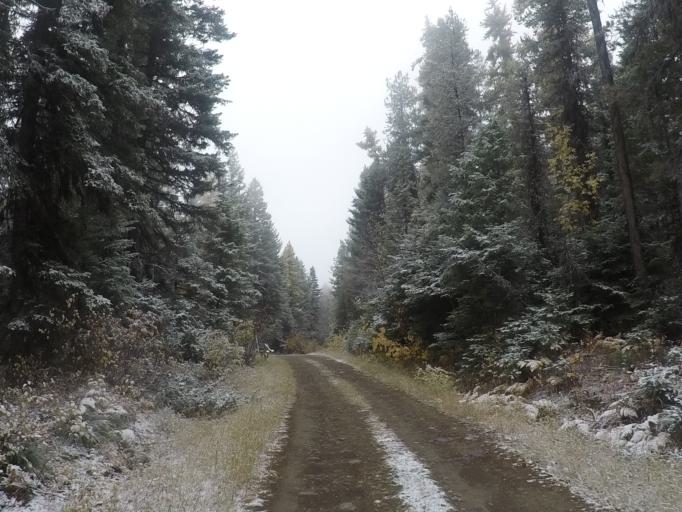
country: US
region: Montana
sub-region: Flathead County
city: Bigfork
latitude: 47.8930
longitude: -113.8753
